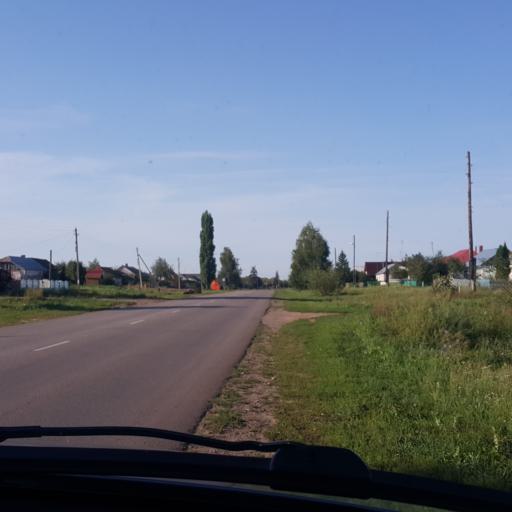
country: RU
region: Tambov
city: Novaya Lyada
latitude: 52.7862
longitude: 41.7664
